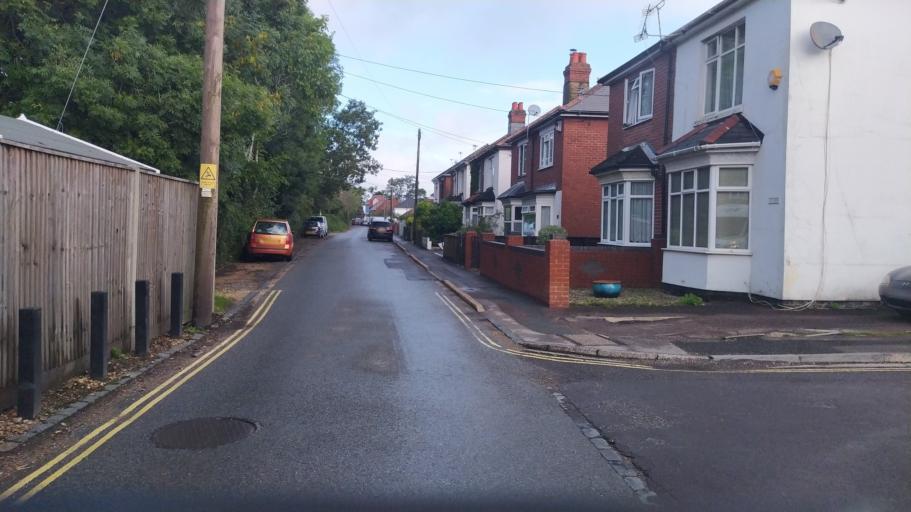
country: GB
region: England
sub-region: Hampshire
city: Totton
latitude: 50.9148
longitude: -1.4894
